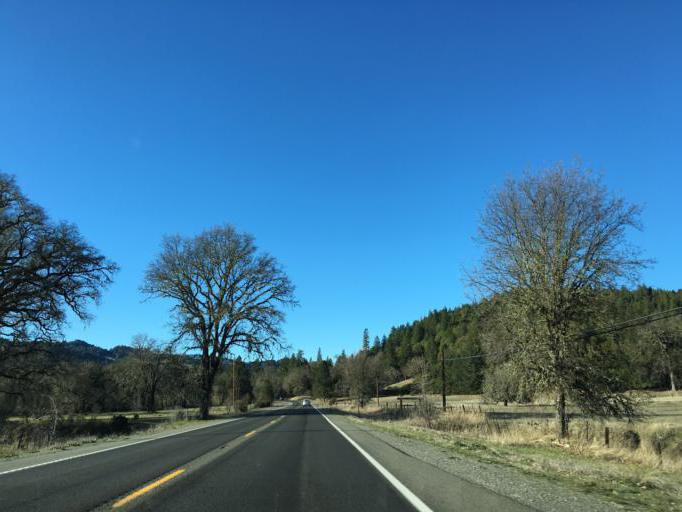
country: US
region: California
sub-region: Mendocino County
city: Laytonville
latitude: 39.7456
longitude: -123.5237
